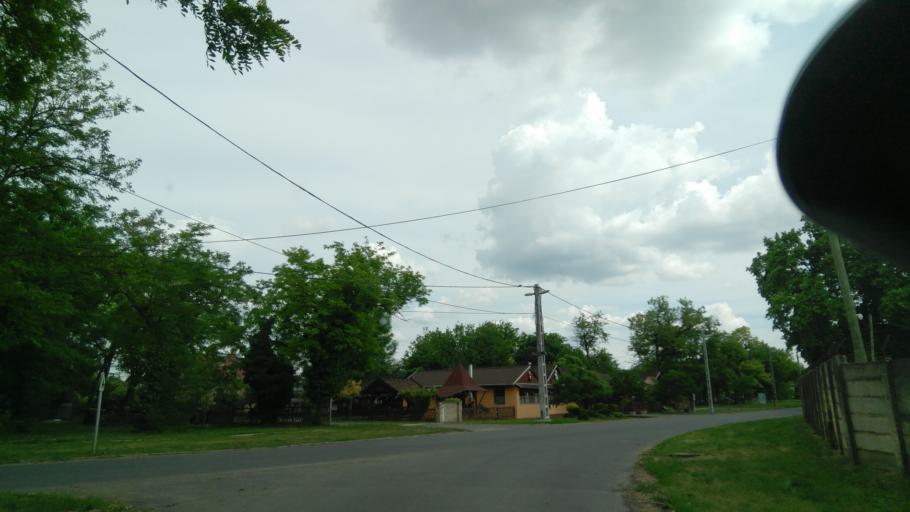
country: HU
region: Bekes
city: Mezohegyes
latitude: 46.3142
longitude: 20.8231
